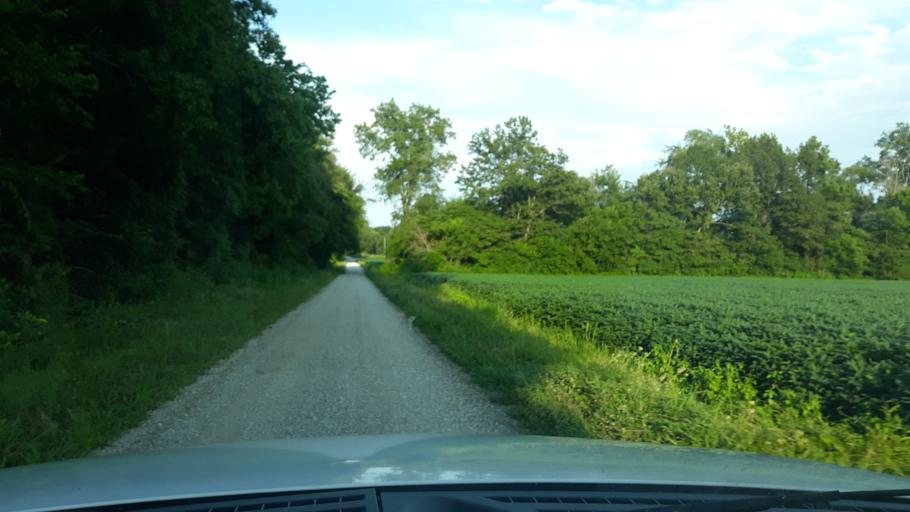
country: US
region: Illinois
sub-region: Saline County
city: Eldorado
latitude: 37.8343
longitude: -88.5066
